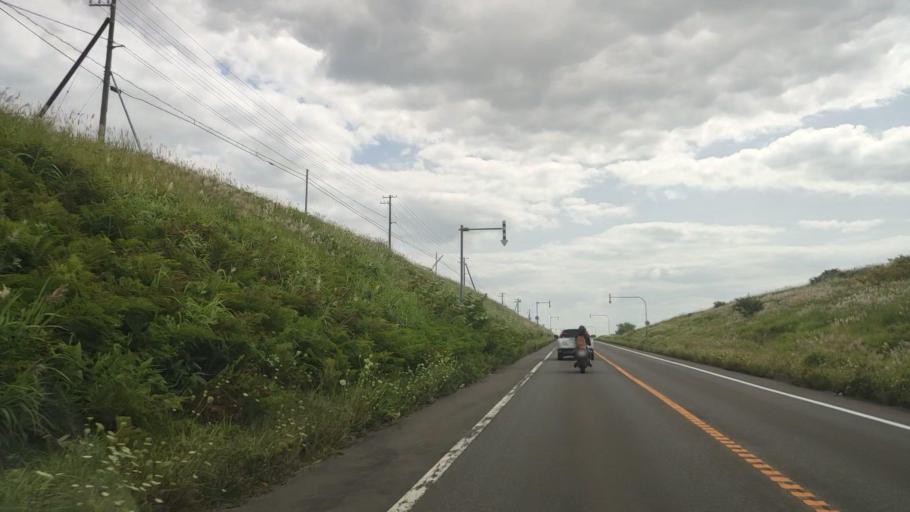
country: JP
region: Hokkaido
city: Rumoi
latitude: 44.5166
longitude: 141.7660
